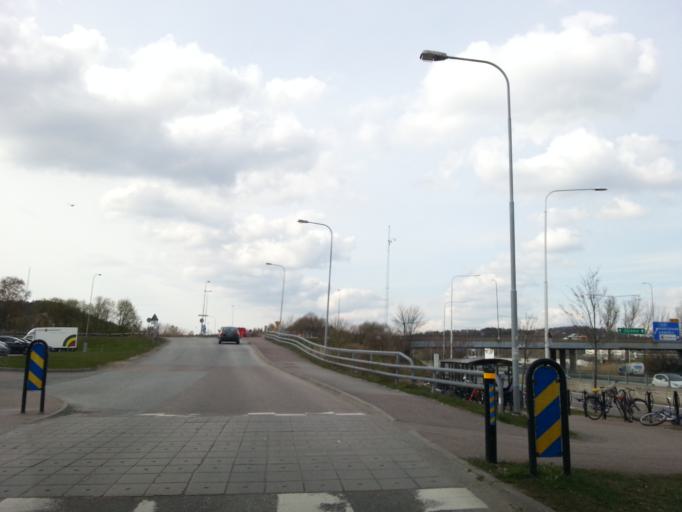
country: SE
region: Vaestra Goetaland
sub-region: Kungalvs Kommun
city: Kungalv
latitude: 57.8707
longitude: 11.9672
